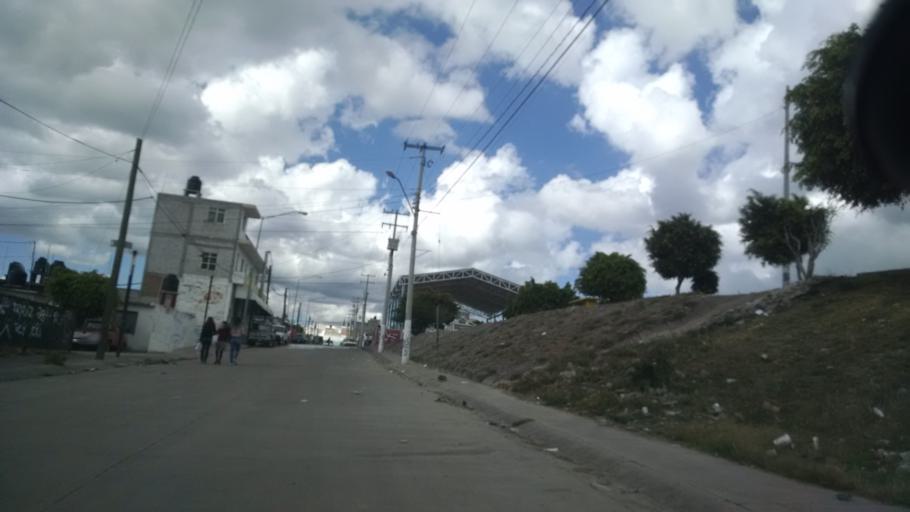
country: MX
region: Guanajuato
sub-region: Leon
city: La Ermita
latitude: 21.1527
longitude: -101.7346
